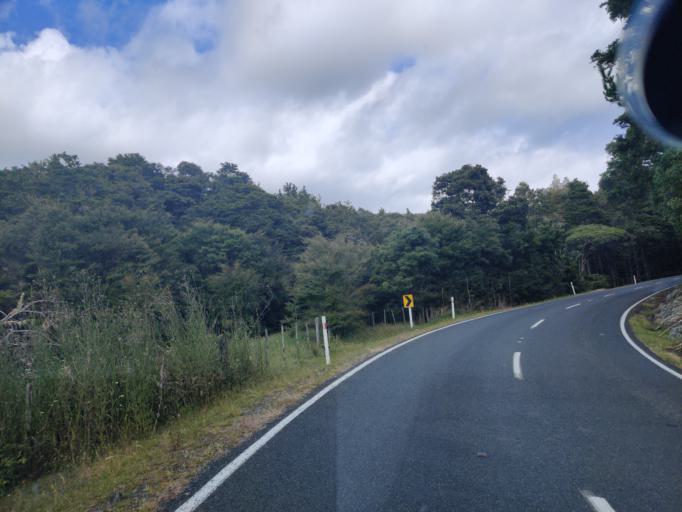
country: NZ
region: Northland
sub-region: Whangarei
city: Ngunguru
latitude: -35.5788
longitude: 174.4155
